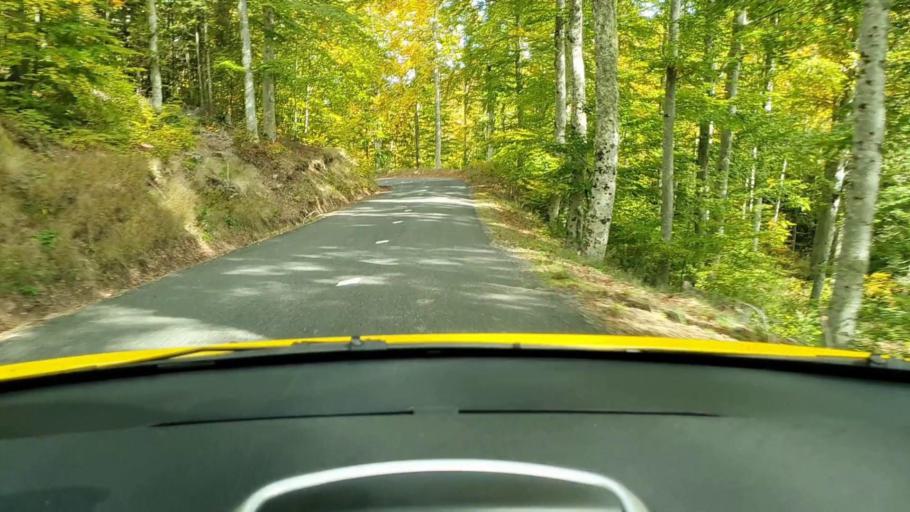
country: FR
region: Languedoc-Roussillon
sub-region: Departement du Gard
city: Valleraugue
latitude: 44.0696
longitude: 3.5686
